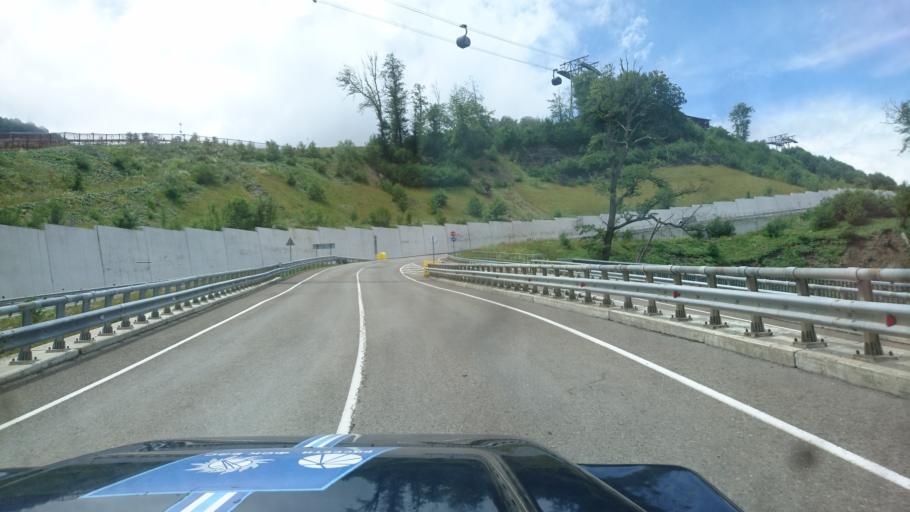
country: RU
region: Krasnodarskiy
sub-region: Sochi City
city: Krasnaya Polyana
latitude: 43.6576
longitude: 40.3286
